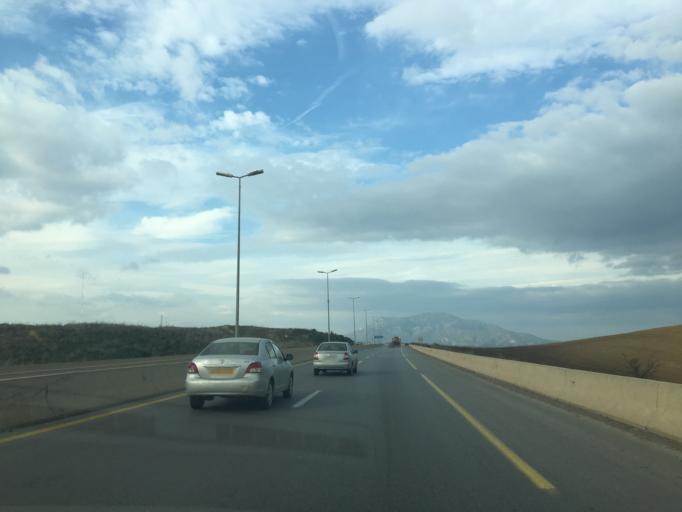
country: DZ
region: Tipaza
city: Tipasa
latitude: 36.5755
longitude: 2.5171
